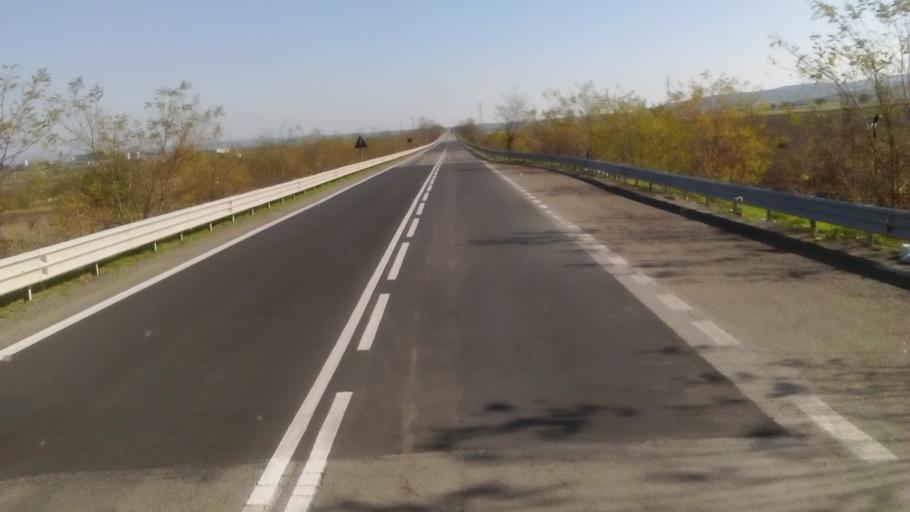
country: IT
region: Basilicate
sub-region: Provincia di Potenza
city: Zona 179
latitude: 41.0815
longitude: 15.6261
